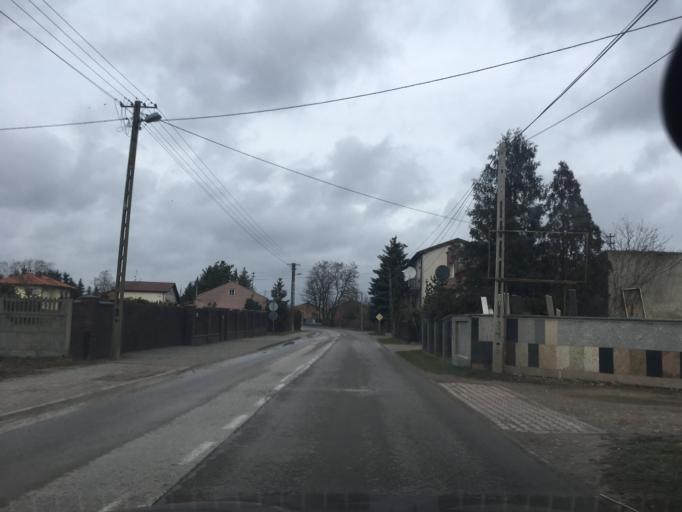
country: PL
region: Masovian Voivodeship
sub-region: Powiat piaseczynski
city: Lesznowola
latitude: 52.1085
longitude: 20.9325
